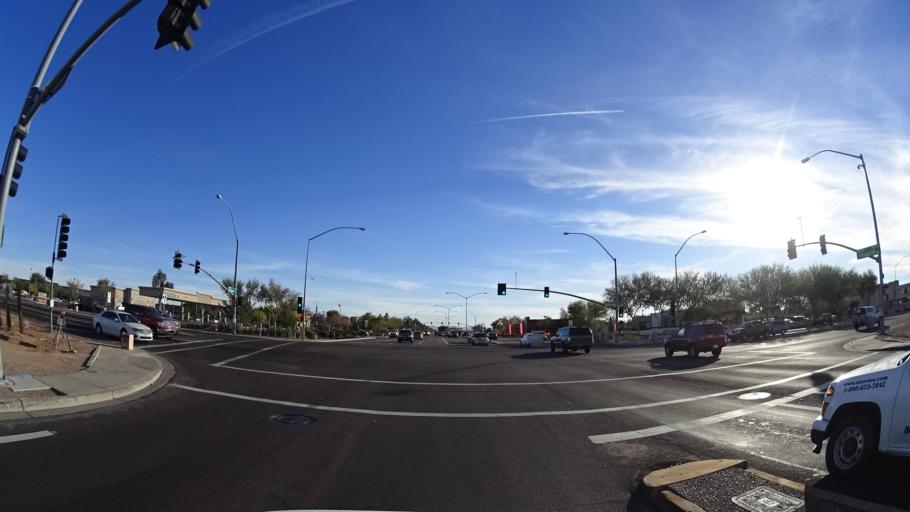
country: US
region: Arizona
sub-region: Pinal County
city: Apache Junction
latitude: 33.3792
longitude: -111.6362
